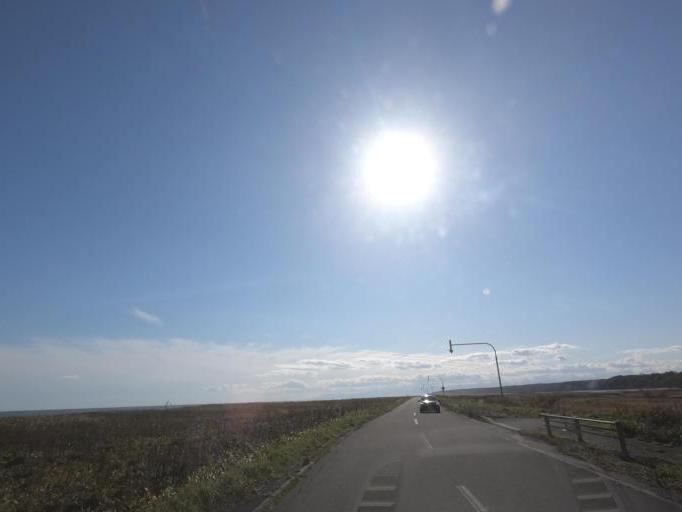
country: JP
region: Hokkaido
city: Obihiro
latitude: 42.5998
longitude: 143.5495
